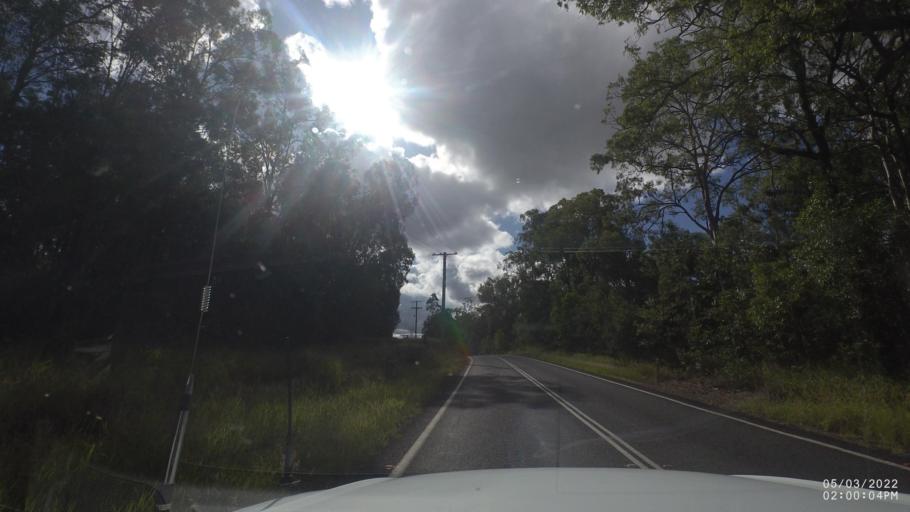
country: AU
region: Queensland
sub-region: Logan
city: Chambers Flat
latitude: -27.8265
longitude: 153.1043
